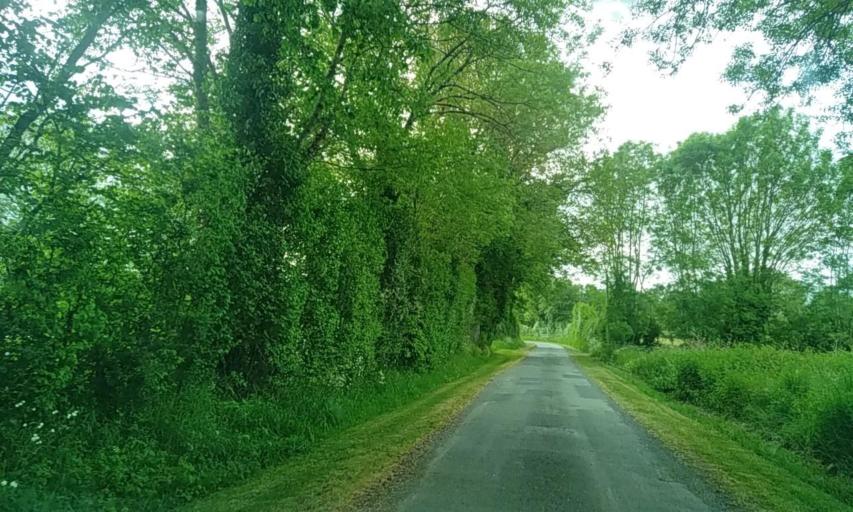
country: FR
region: Poitou-Charentes
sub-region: Departement des Deux-Sevres
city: Boisme
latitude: 46.7668
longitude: -0.4247
